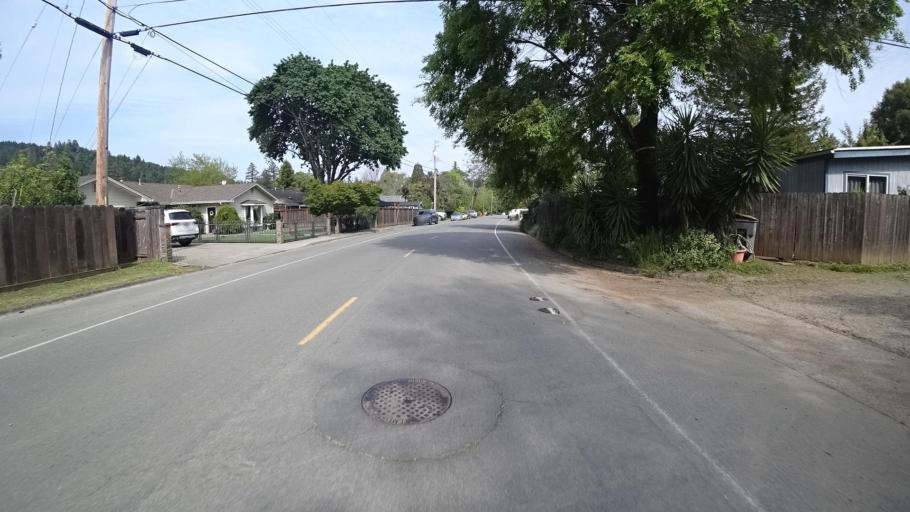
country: US
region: California
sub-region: Humboldt County
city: Redway
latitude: 40.1176
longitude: -123.8281
